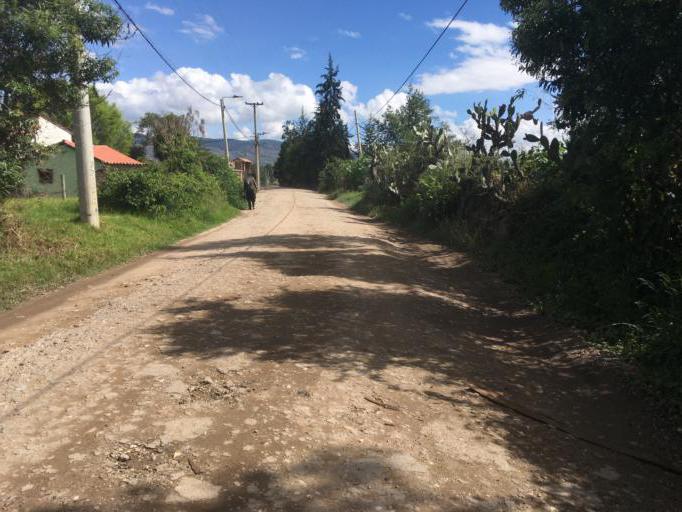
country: CO
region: Boyaca
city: Firavitoba
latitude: 5.6610
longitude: -72.9584
